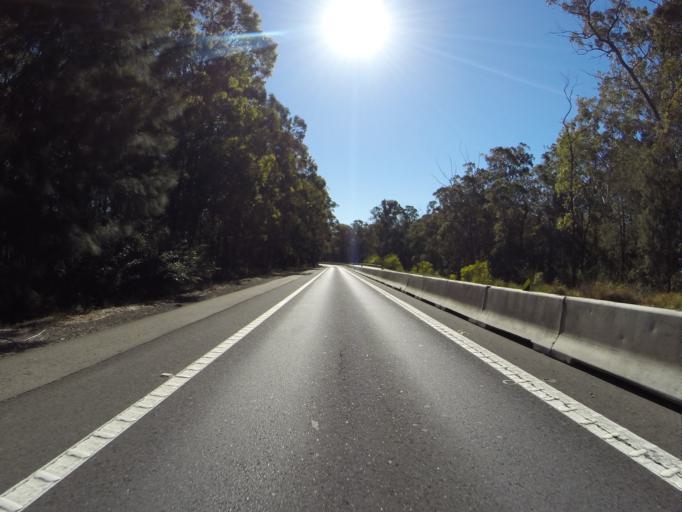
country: AU
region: New South Wales
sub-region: Wollondilly
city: Douglas Park
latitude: -34.2785
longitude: 150.7146
